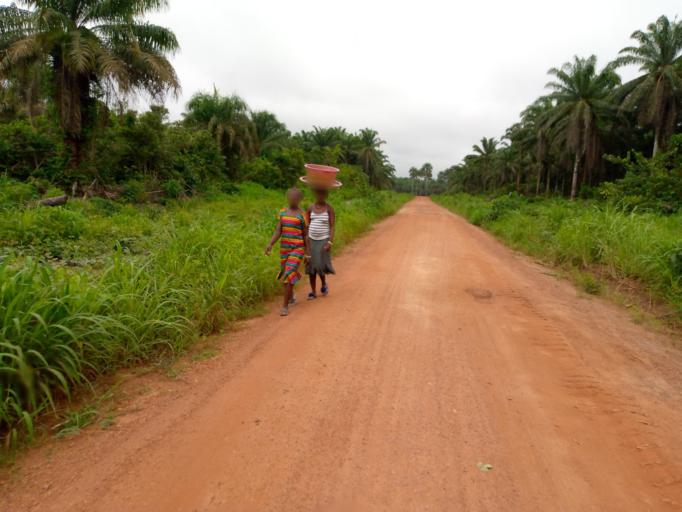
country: SL
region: Southern Province
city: Sumbuya
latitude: 7.5734
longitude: -12.0873
